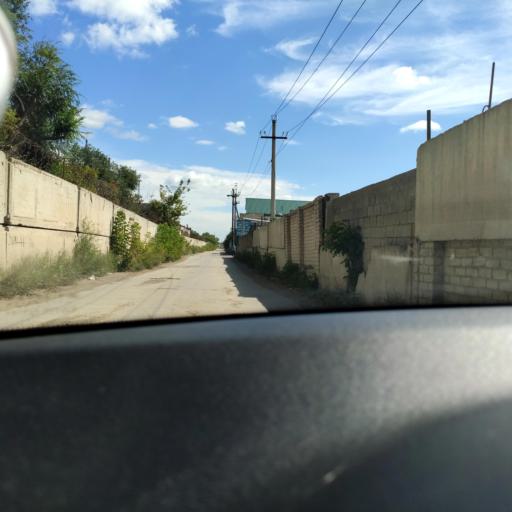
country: RU
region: Samara
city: Samara
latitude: 53.2012
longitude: 50.2700
